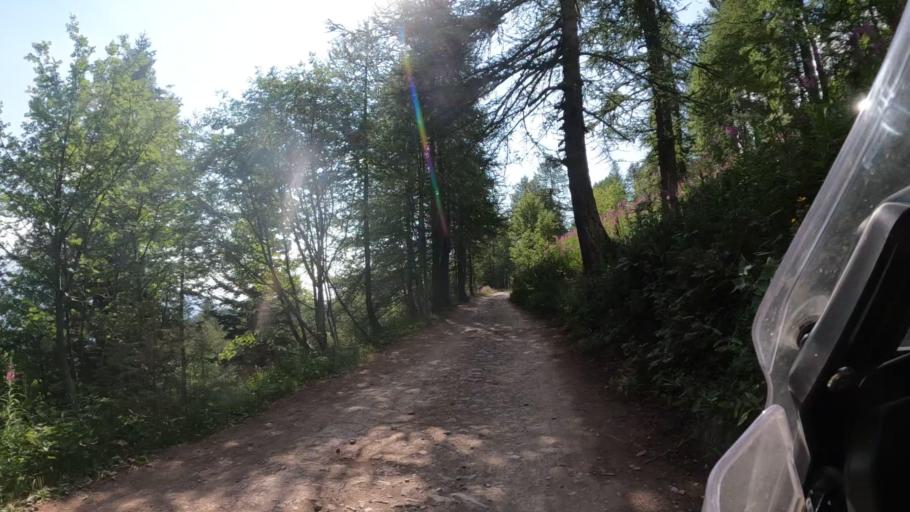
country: IT
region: Piedmont
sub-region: Provincia di Cuneo
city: Briga Alta
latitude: 44.1139
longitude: 7.7022
